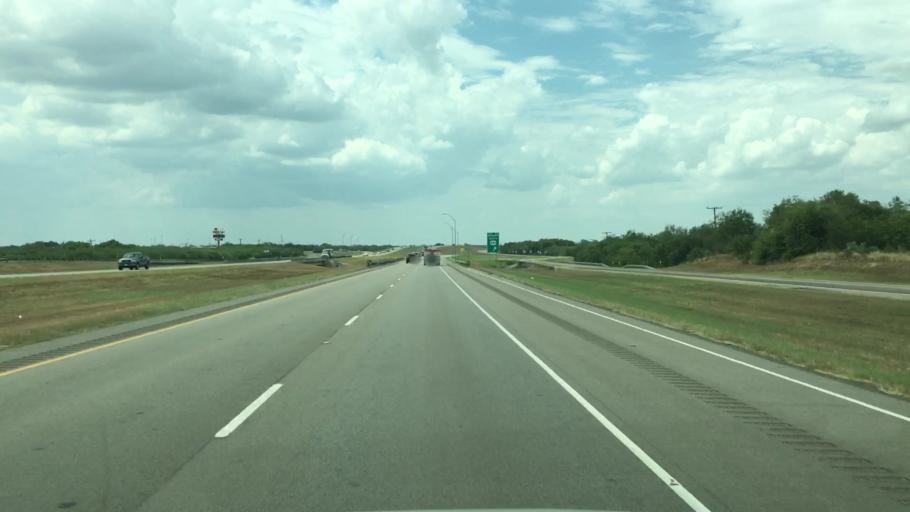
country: US
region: Texas
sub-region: Live Oak County
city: Three Rivers
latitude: 28.5174
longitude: -98.1767
